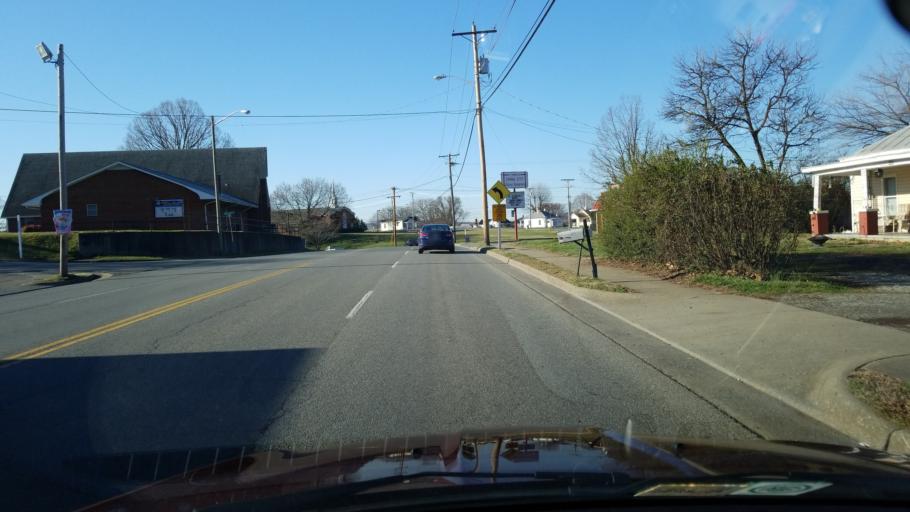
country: US
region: Virginia
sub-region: Franklin County
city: Rocky Mount
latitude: 37.0054
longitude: -79.8953
